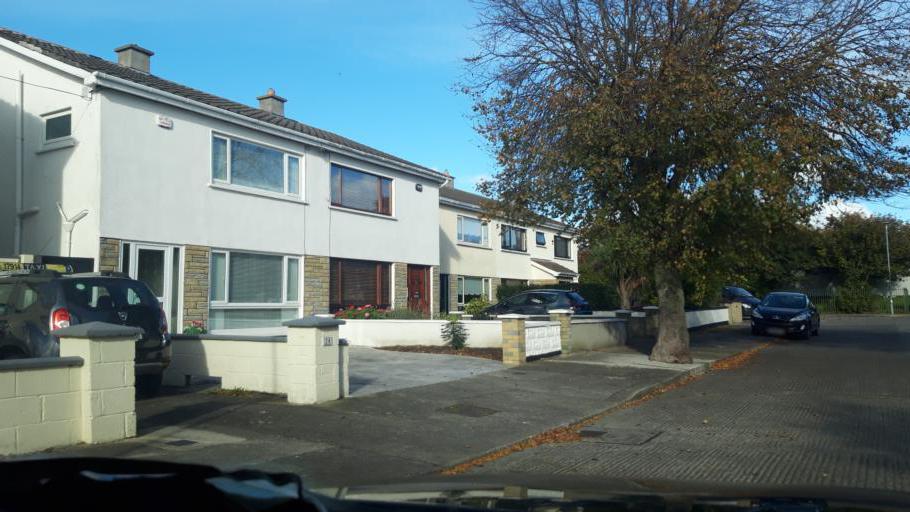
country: IE
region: Leinster
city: Artane
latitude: 53.3816
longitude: -6.2141
